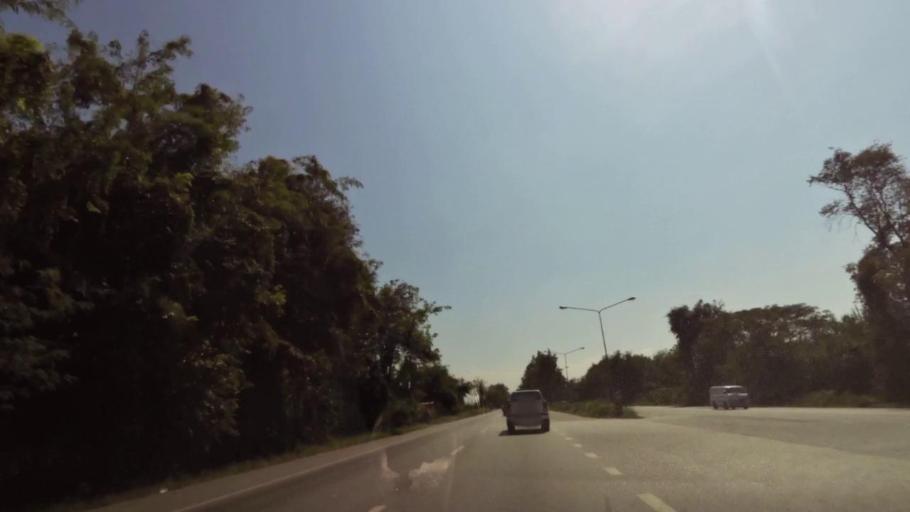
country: TH
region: Nakhon Sawan
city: Kao Liao
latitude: 15.8393
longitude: 100.1174
